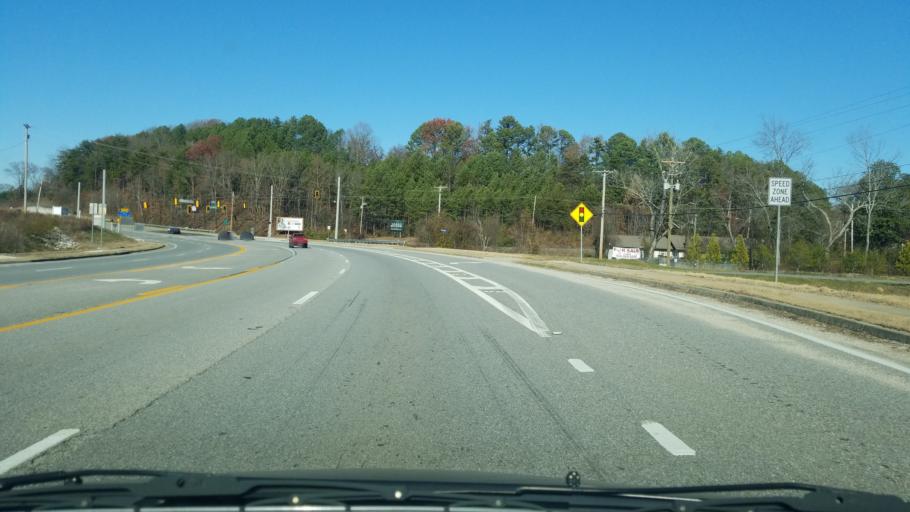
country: US
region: Georgia
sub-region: Catoosa County
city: Indian Springs
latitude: 34.9846
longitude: -85.1872
